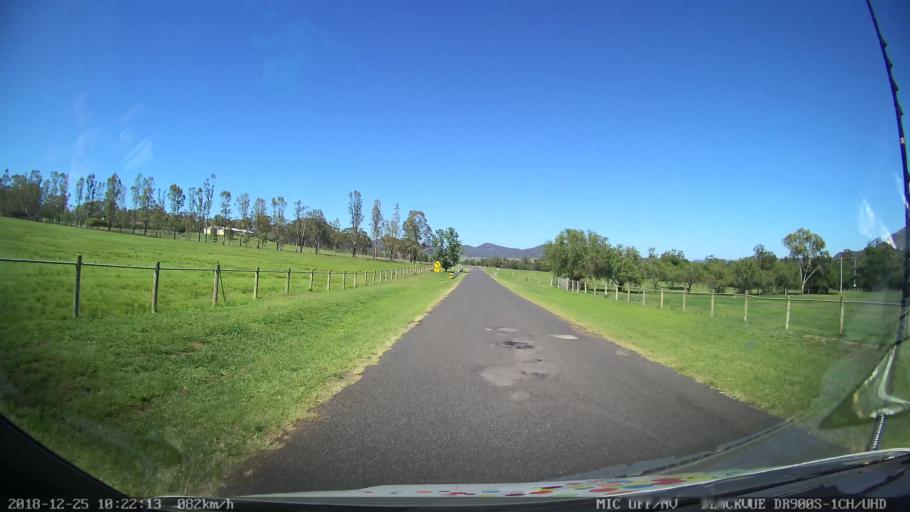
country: AU
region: New South Wales
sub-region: Muswellbrook
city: Denman
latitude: -32.3748
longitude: 150.5350
